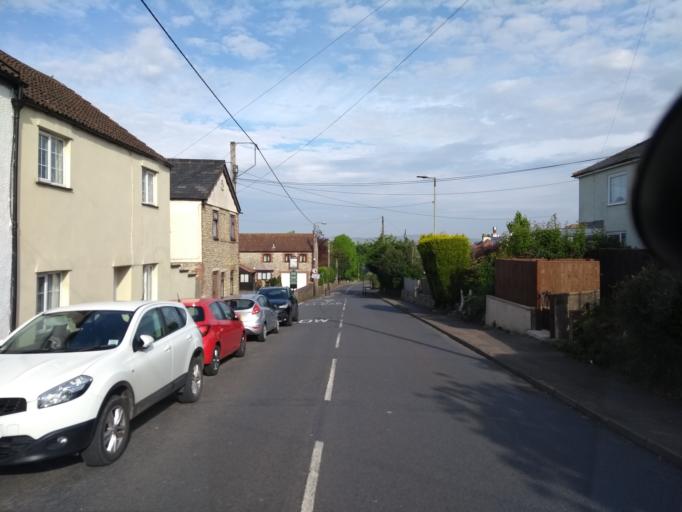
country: GB
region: England
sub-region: Devon
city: Axminster
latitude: 50.7801
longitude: -2.9904
